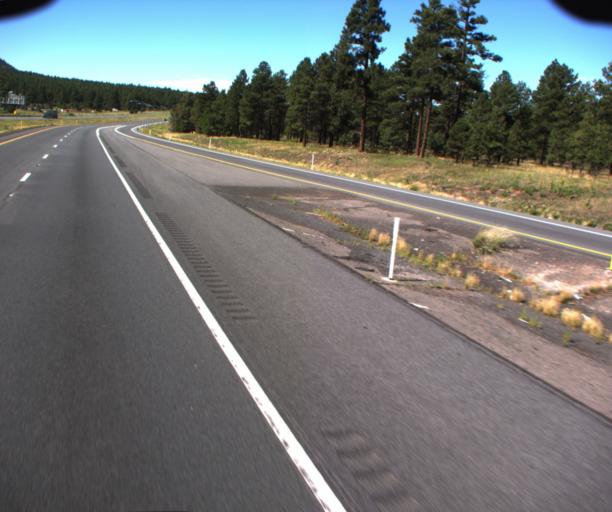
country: US
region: Arizona
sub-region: Coconino County
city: Williams
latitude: 35.2421
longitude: -112.2173
